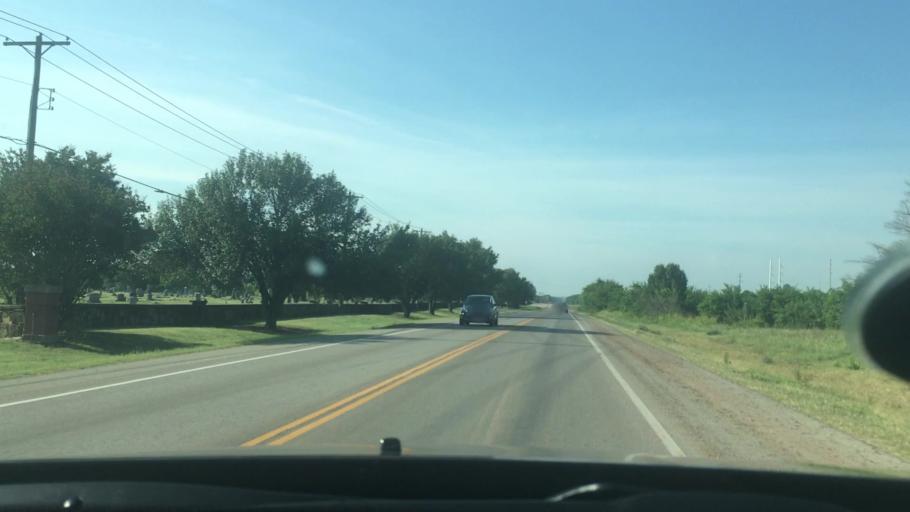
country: US
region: Oklahoma
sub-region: Garvin County
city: Pauls Valley
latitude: 34.7145
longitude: -97.2130
